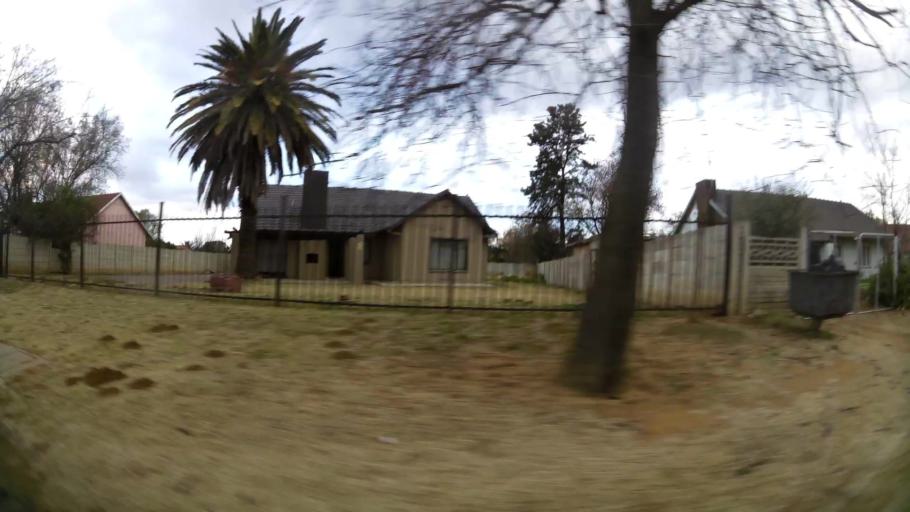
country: ZA
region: Orange Free State
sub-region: Lejweleputswa District Municipality
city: Welkom
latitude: -27.9679
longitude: 26.7221
